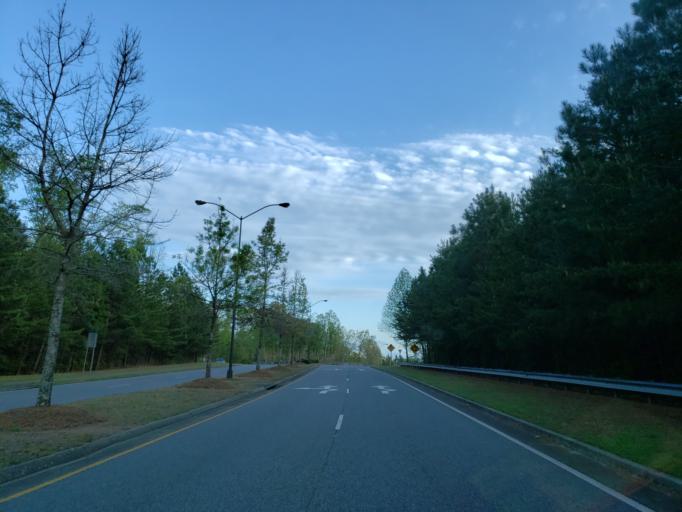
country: US
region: Georgia
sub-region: Cherokee County
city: Canton
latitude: 34.2811
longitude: -84.4690
